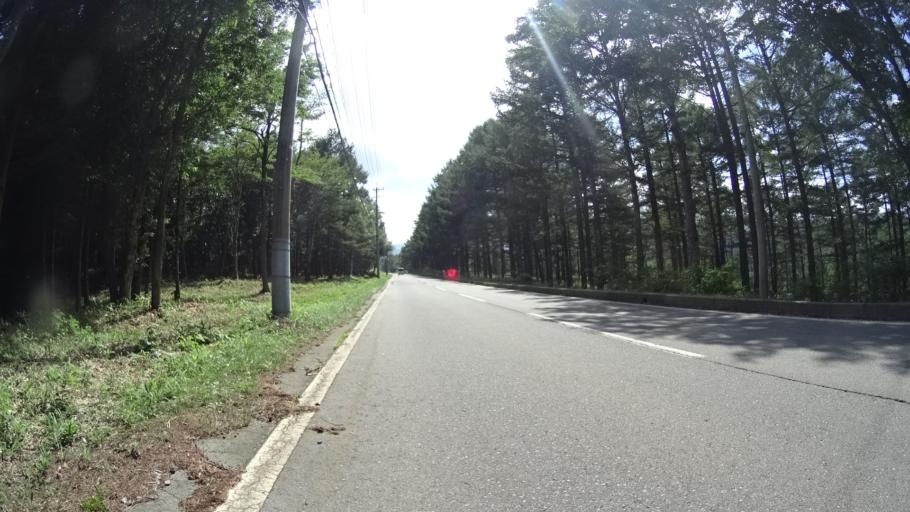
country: JP
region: Nagano
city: Saku
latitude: 36.0543
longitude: 138.4235
